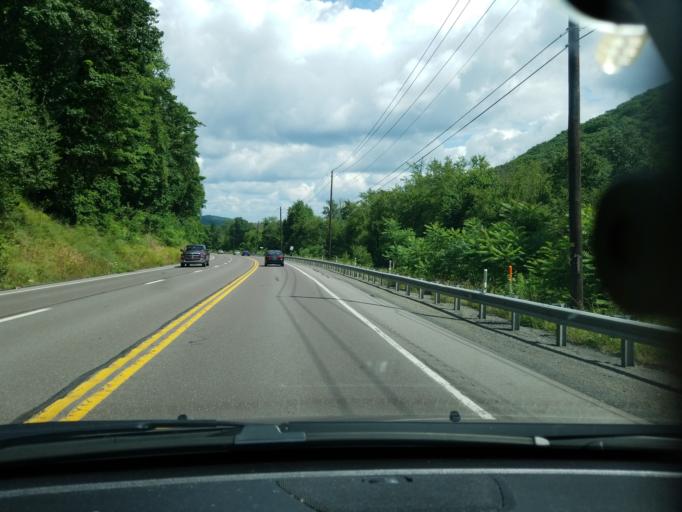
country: US
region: Pennsylvania
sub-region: Northumberland County
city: Kulpmont
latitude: 40.8264
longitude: -76.5028
